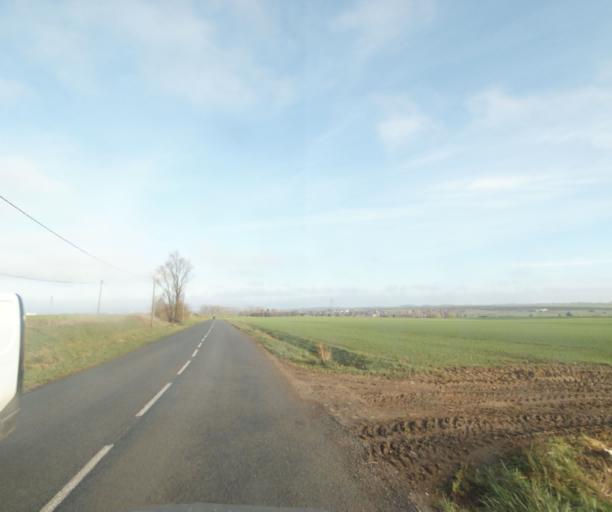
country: FR
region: Nord-Pas-de-Calais
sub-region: Departement du Nord
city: Thiant
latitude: 50.2785
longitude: 3.4390
